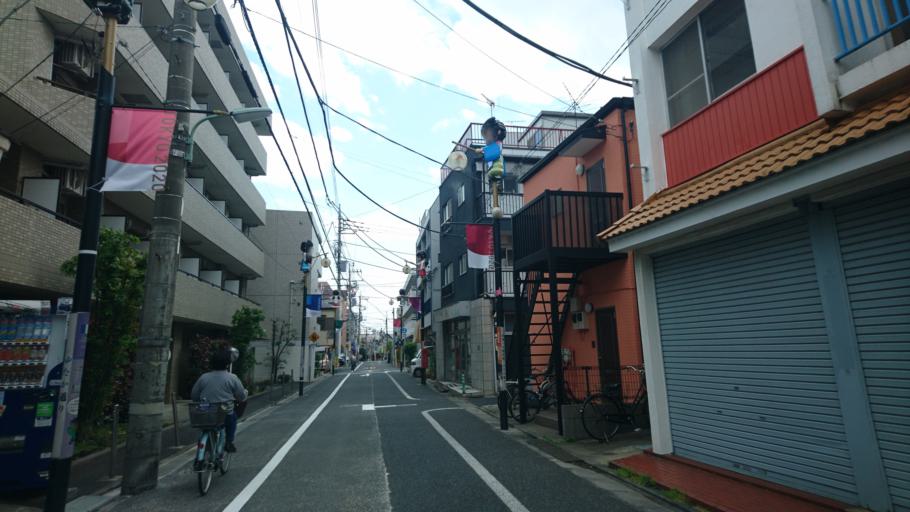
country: JP
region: Kanagawa
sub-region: Kawasaki-shi
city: Kawasaki
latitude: 35.6050
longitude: 139.7184
